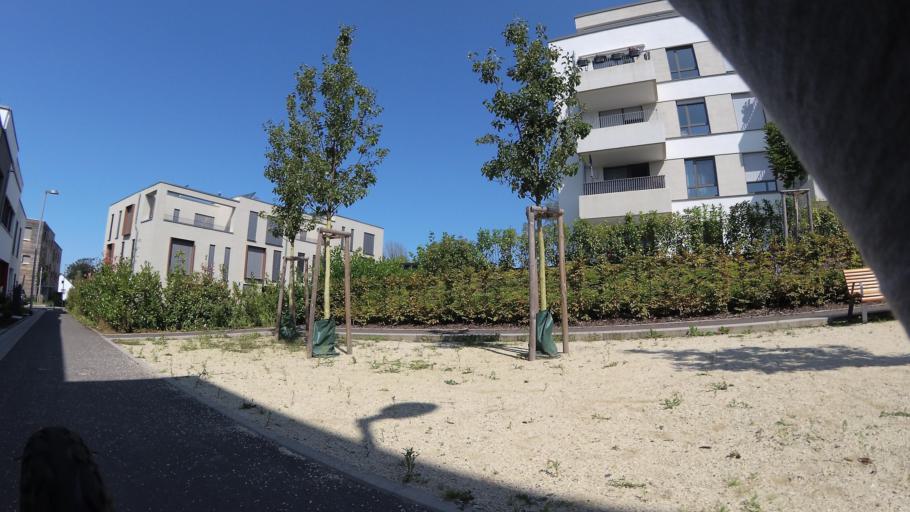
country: DE
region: Saarland
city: Saarbrucken
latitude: 49.2231
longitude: 6.9779
